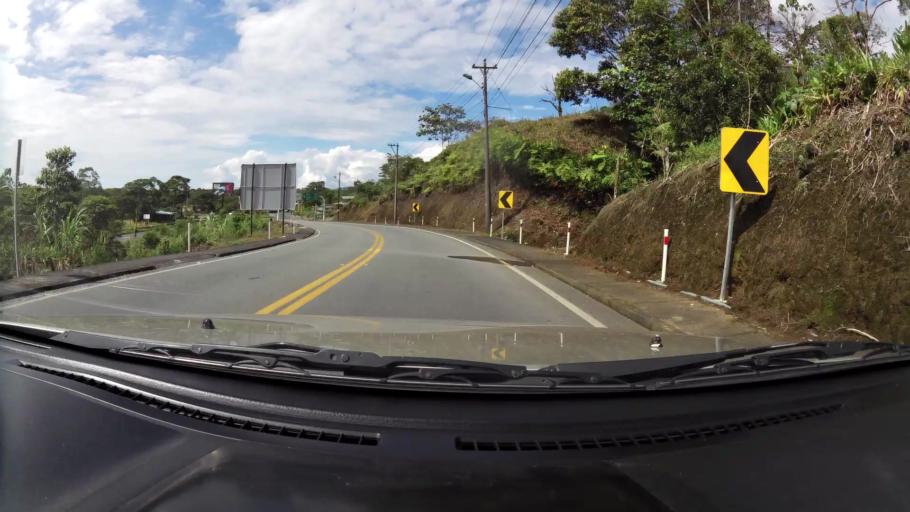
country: EC
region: Pastaza
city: Puyo
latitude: -1.5003
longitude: -78.0242
